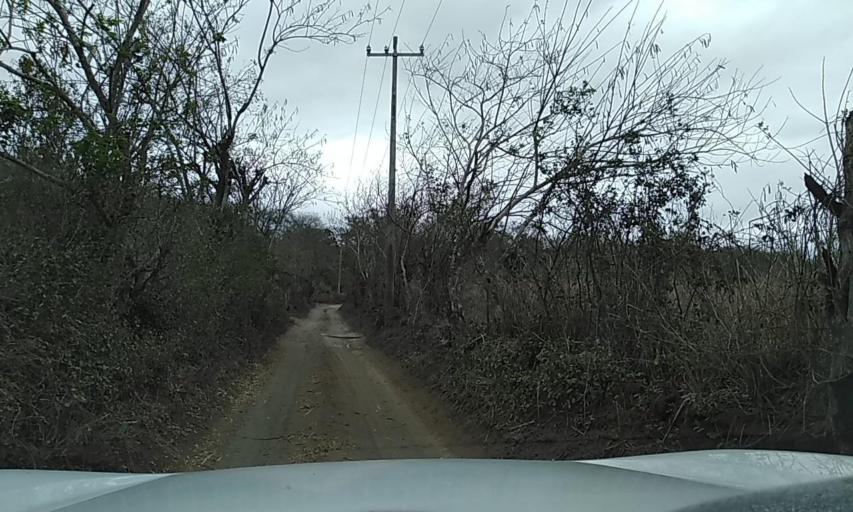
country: MX
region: Veracruz
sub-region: Veracruz
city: Delfino Victoria (Santa Fe)
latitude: 19.2747
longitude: -96.3099
